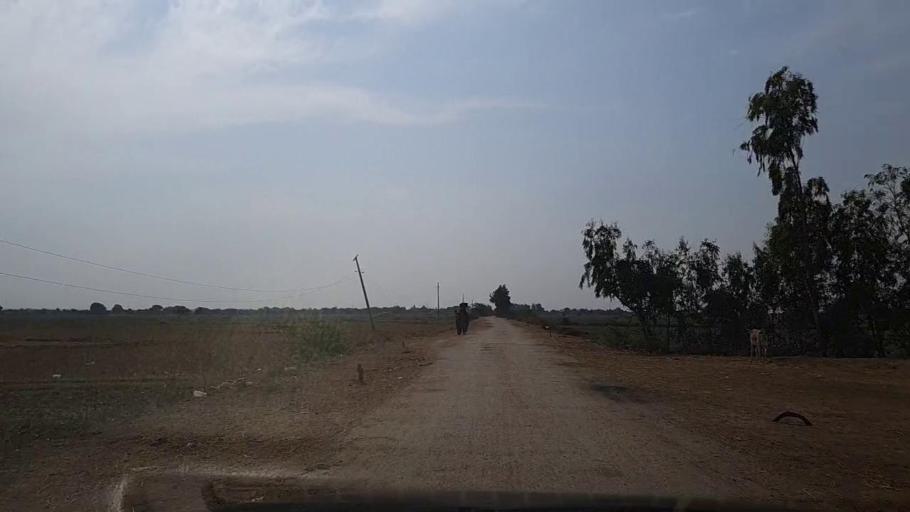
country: PK
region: Sindh
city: Thatta
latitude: 24.7982
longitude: 67.8759
